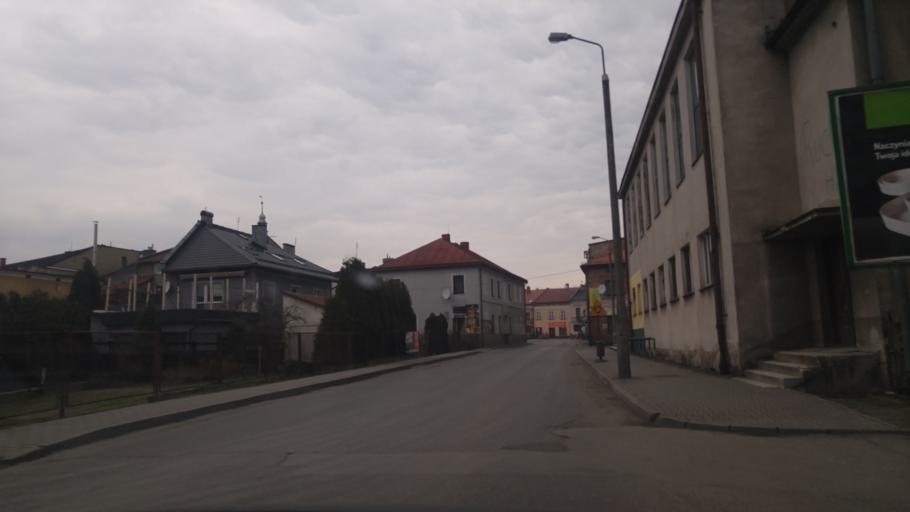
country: PL
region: Silesian Voivodeship
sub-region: Powiat cieszynski
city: Strumien
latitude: 49.9162
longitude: 18.7645
